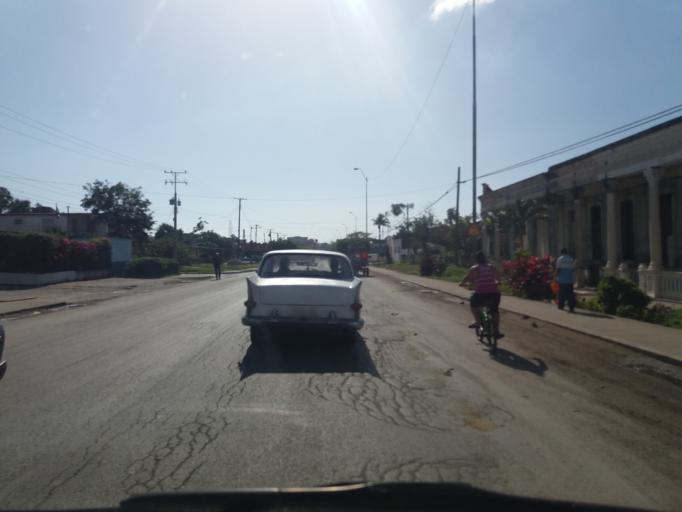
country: CU
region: Cienfuegos
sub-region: Municipio de Cienfuegos
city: Cienfuegos
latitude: 22.1535
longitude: -80.4365
